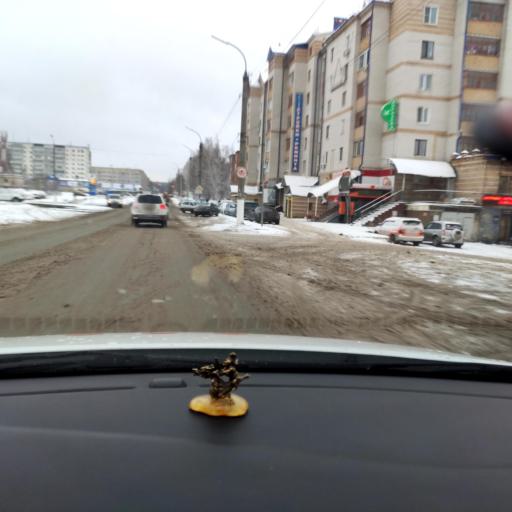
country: RU
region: Tatarstan
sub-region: Zelenodol'skiy Rayon
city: Zelenodolsk
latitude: 55.8587
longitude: 48.5571
